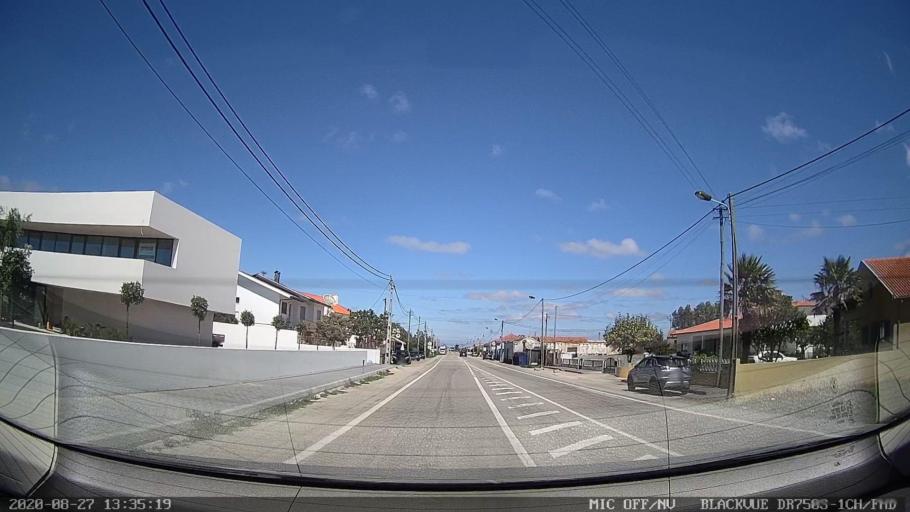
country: PT
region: Coimbra
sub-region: Mira
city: Mira
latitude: 40.4646
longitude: -8.7000
